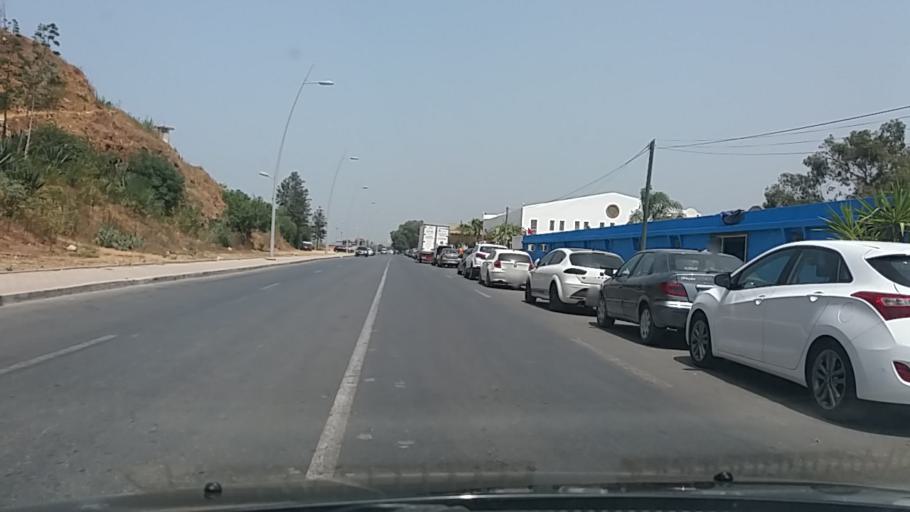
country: MA
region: Gharb-Chrarda-Beni Hssen
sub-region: Kenitra Province
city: Kenitra
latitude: 34.2708
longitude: -6.5915
